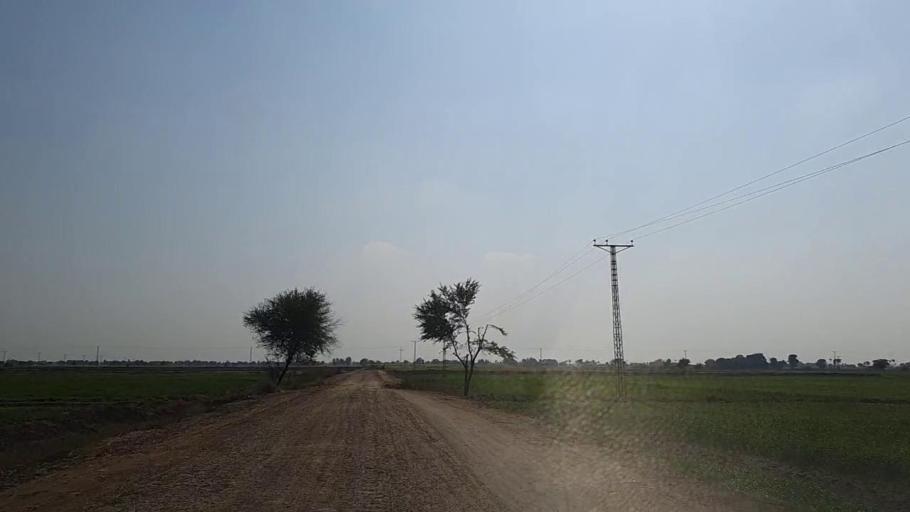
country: PK
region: Sindh
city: Daur
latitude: 26.4457
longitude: 68.2345
